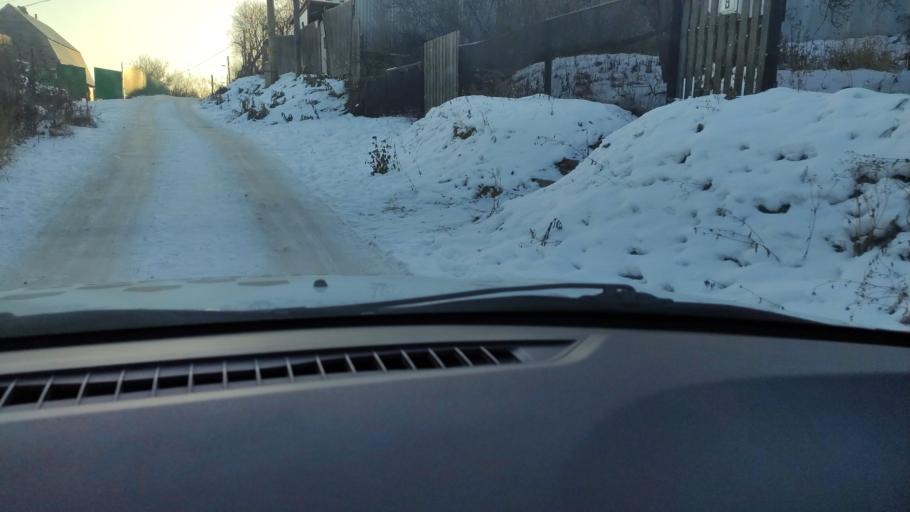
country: RU
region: Perm
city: Perm
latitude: 58.0341
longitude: 56.3307
